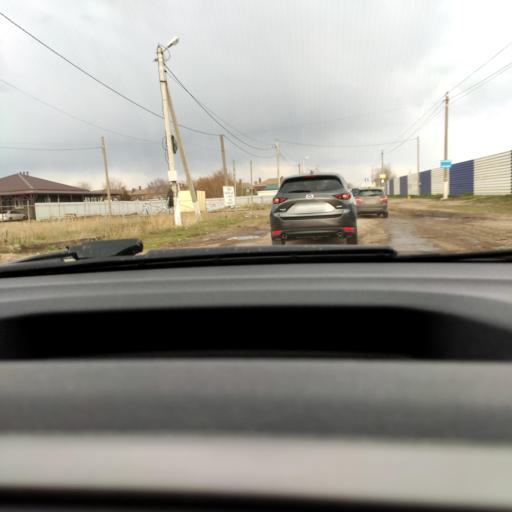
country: RU
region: Samara
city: Podstepki
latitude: 53.5149
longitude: 49.2206
